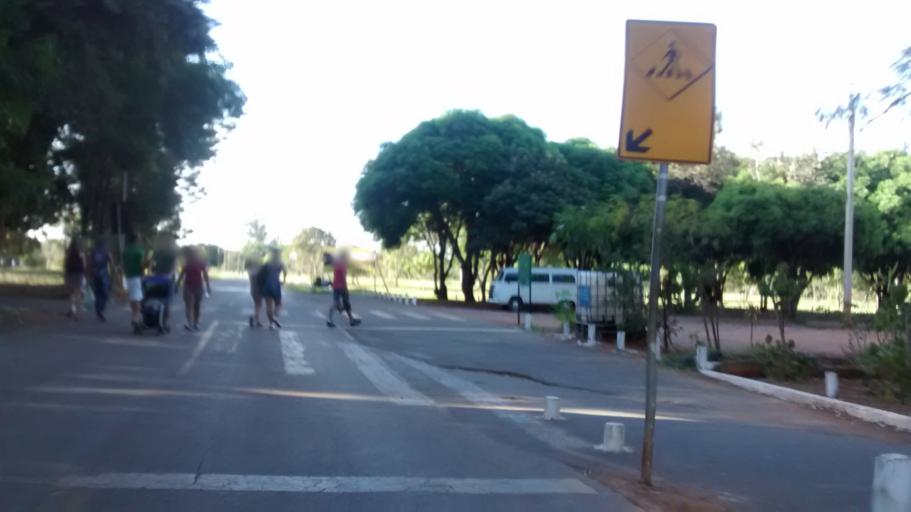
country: BR
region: Federal District
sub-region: Brasilia
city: Brasilia
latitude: -15.8365
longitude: -48.0249
